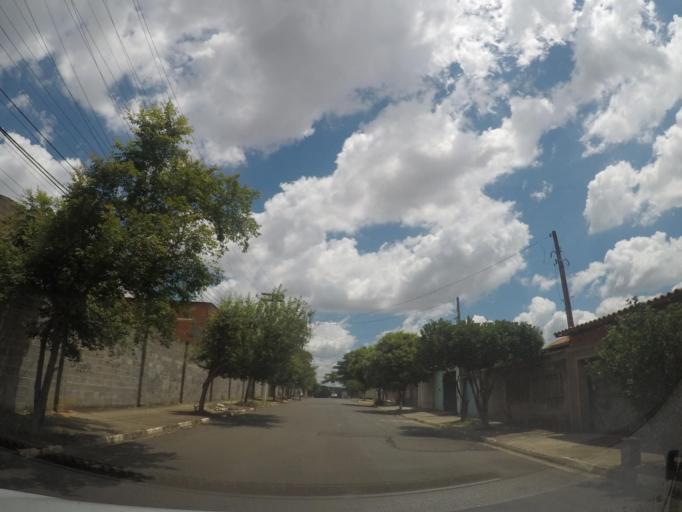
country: BR
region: Sao Paulo
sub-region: Hortolandia
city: Hortolandia
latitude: -22.8186
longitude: -47.2046
